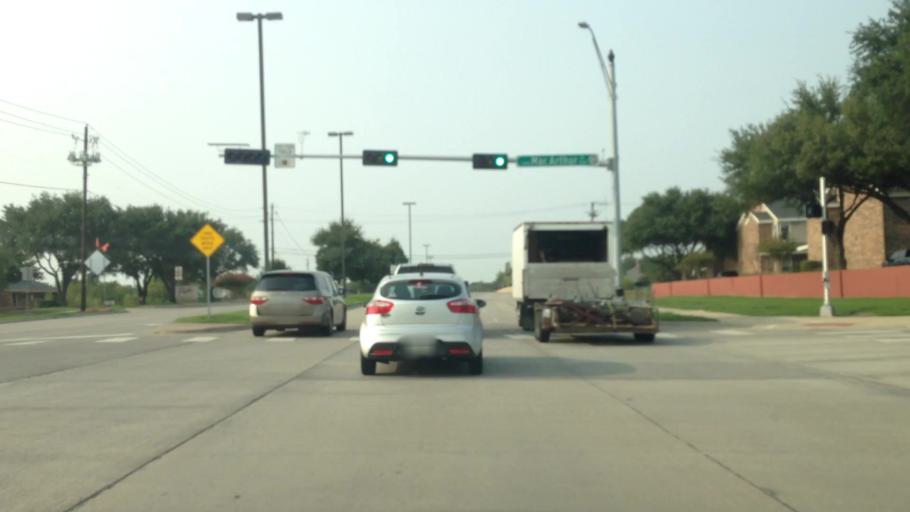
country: US
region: Texas
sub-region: Dallas County
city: Carrollton
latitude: 32.9846
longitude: -96.9202
